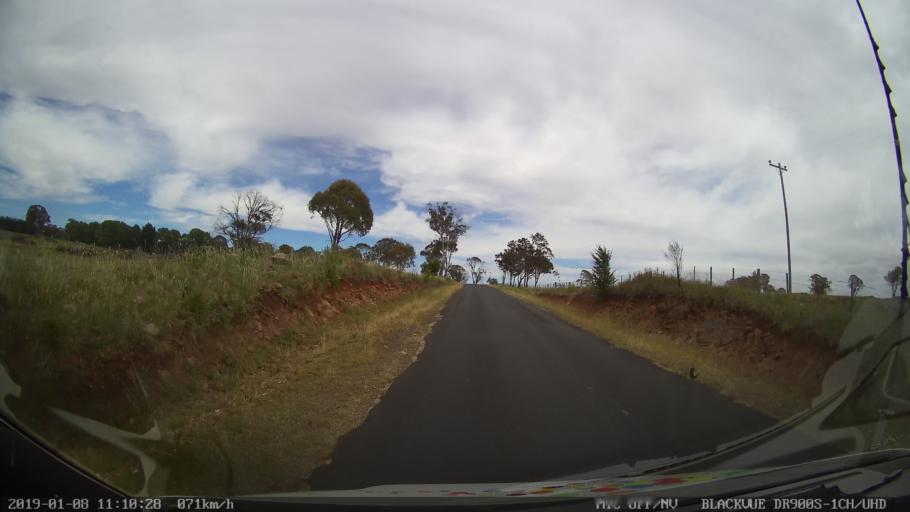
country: AU
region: New South Wales
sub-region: Guyra
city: Guyra
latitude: -30.2257
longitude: 151.6360
